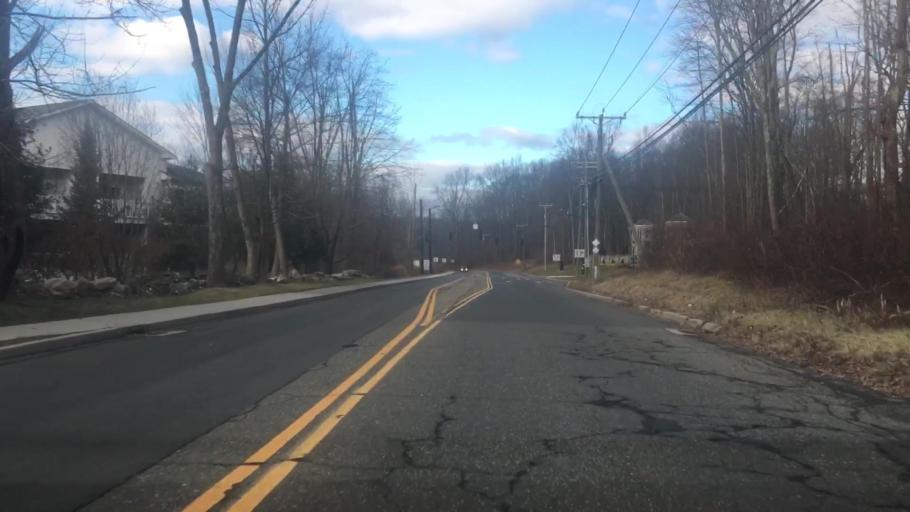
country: US
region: New York
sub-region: Putnam County
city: Peach Lake
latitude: 41.3817
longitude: -73.5360
